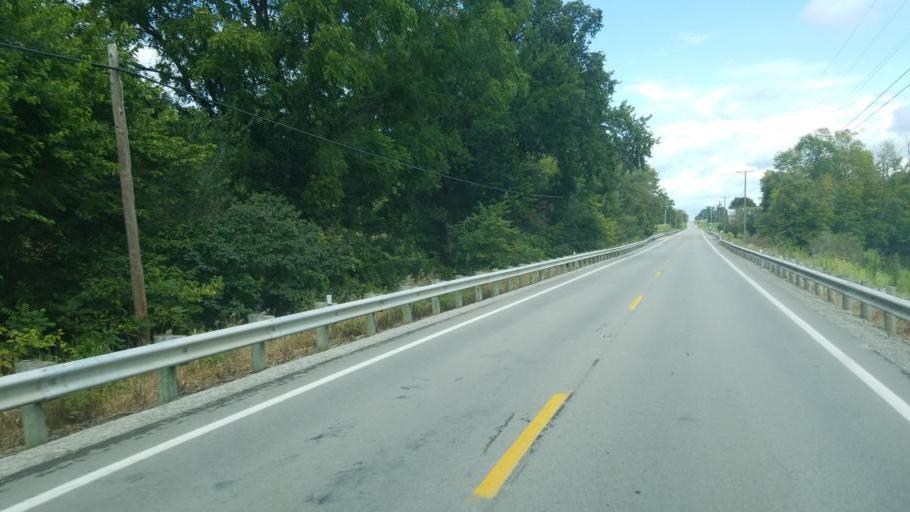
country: US
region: Ohio
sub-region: Seneca County
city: Tiffin
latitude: 41.0632
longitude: -83.0153
